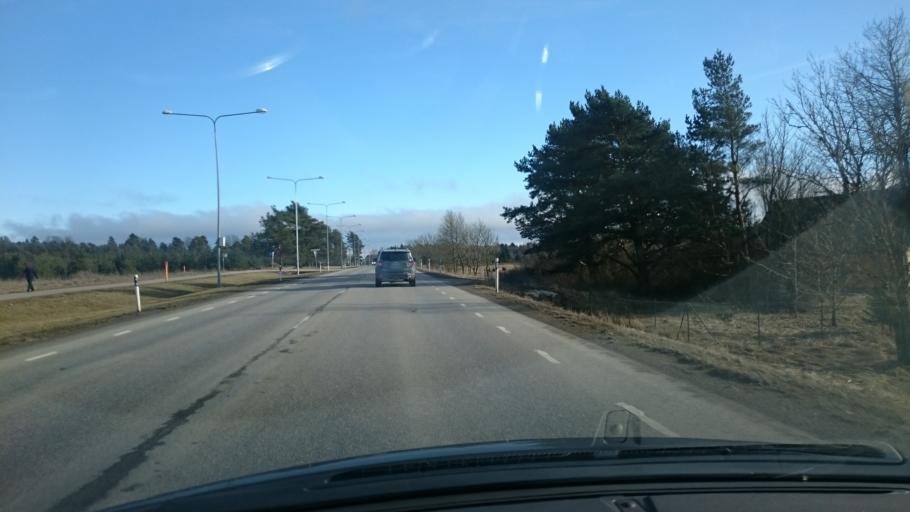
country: EE
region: Harju
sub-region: Harku vald
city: Tabasalu
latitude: 59.4407
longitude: 24.4949
